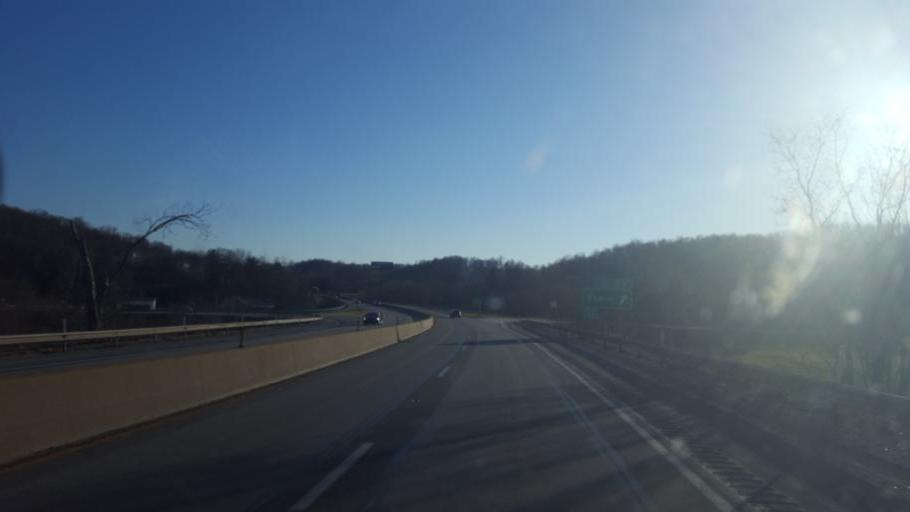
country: US
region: Pennsylvania
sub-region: Westmoreland County
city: New Stanton
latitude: 40.2106
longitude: -79.6752
